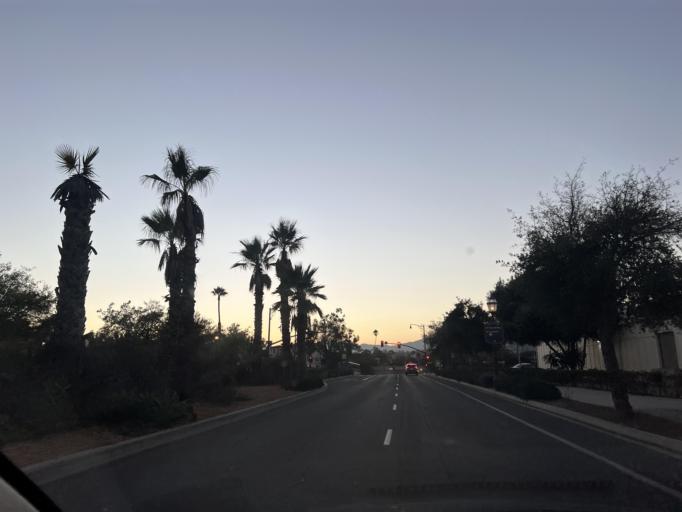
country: US
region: California
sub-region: Santa Barbara County
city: Santa Barbara
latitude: 34.4167
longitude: -119.6878
